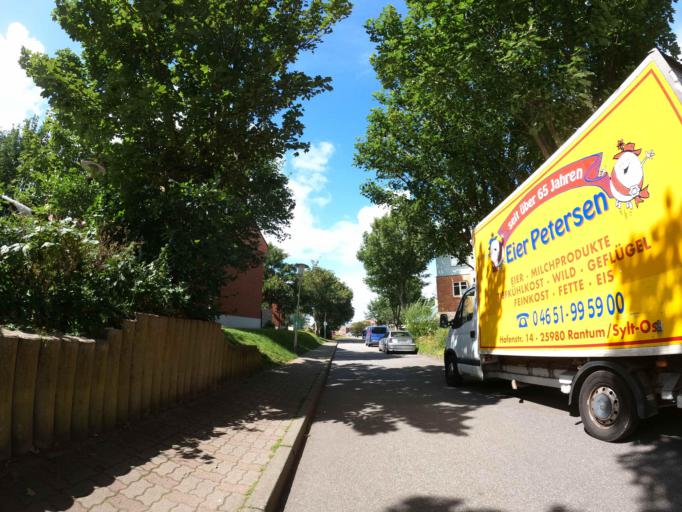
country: DE
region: Schleswig-Holstein
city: Westerland
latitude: 54.9016
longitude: 8.3131
